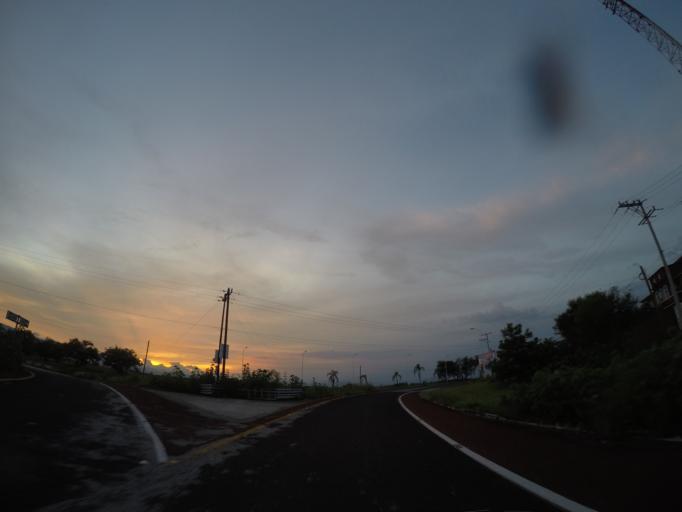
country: MX
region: Morelos
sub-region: Jojutla
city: Tehuixtla
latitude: 18.5896
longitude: -99.2590
